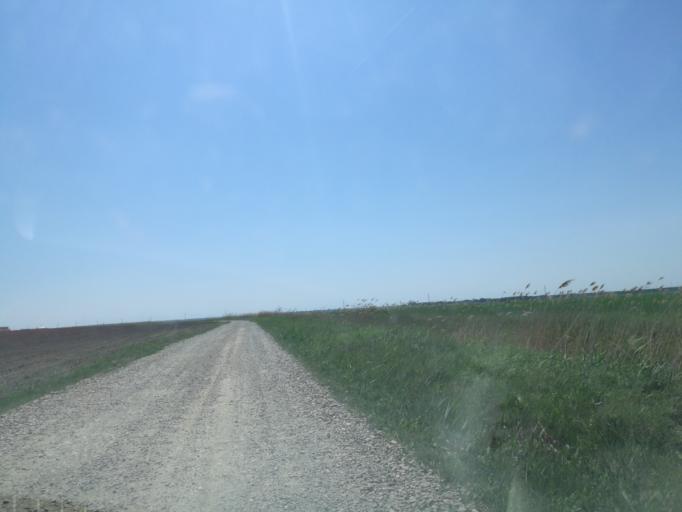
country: RO
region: Ialomita
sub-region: Comuna Adancata
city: Adancata
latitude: 44.7851
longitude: 26.4633
